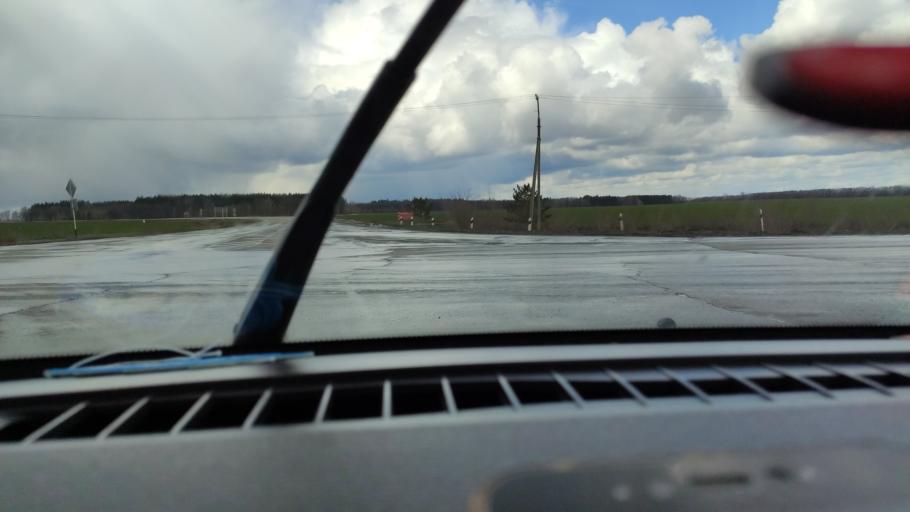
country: RU
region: Samara
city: Povolzhskiy
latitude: 53.8060
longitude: 49.7926
